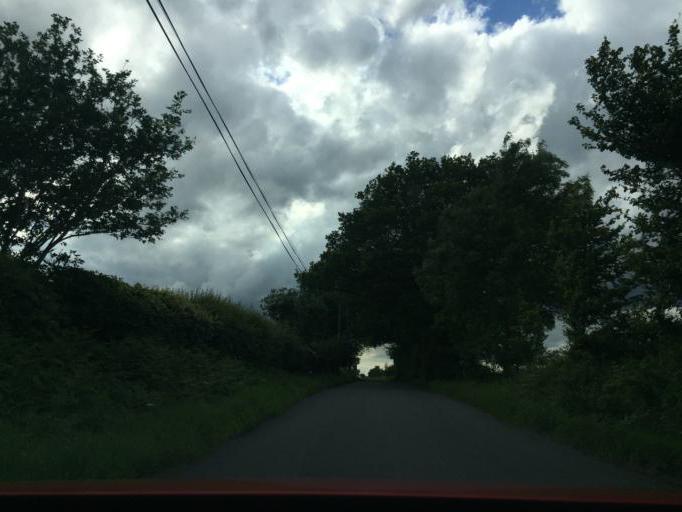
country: GB
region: England
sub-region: Hertfordshire
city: Harpenden
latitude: 51.8561
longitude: -0.3341
